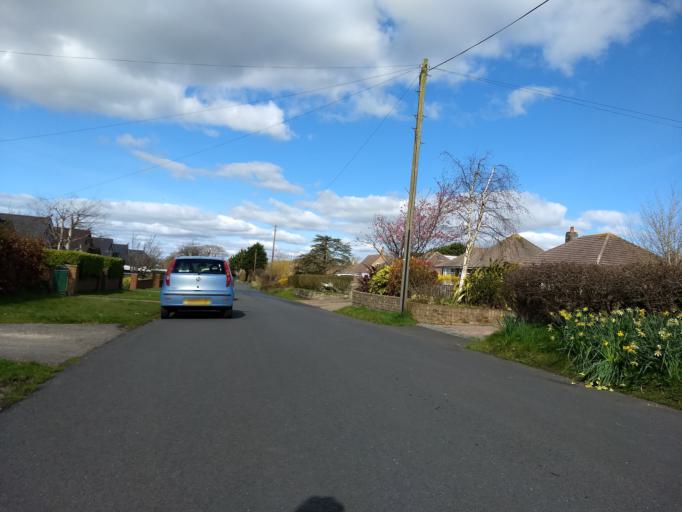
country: GB
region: England
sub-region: Isle of Wight
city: East Cowes
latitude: 50.7366
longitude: -1.2643
